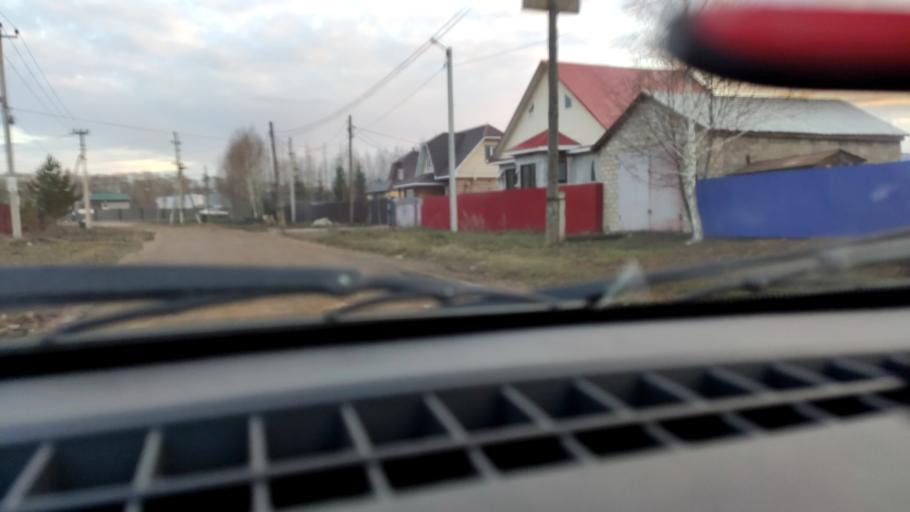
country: RU
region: Bashkortostan
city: Iglino
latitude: 54.8205
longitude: 56.3769
